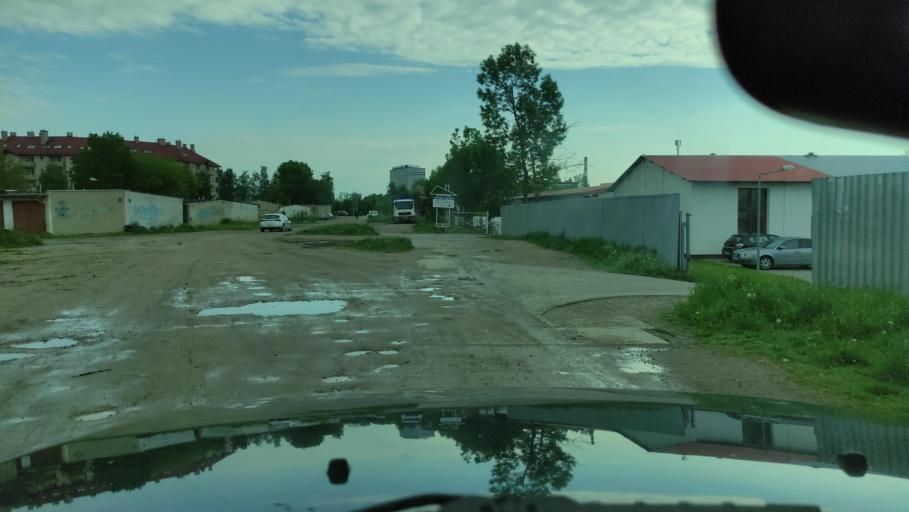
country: PL
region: Warmian-Masurian Voivodeship
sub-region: Powiat olsztynski
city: Olsztyn
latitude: 53.7671
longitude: 20.5102
